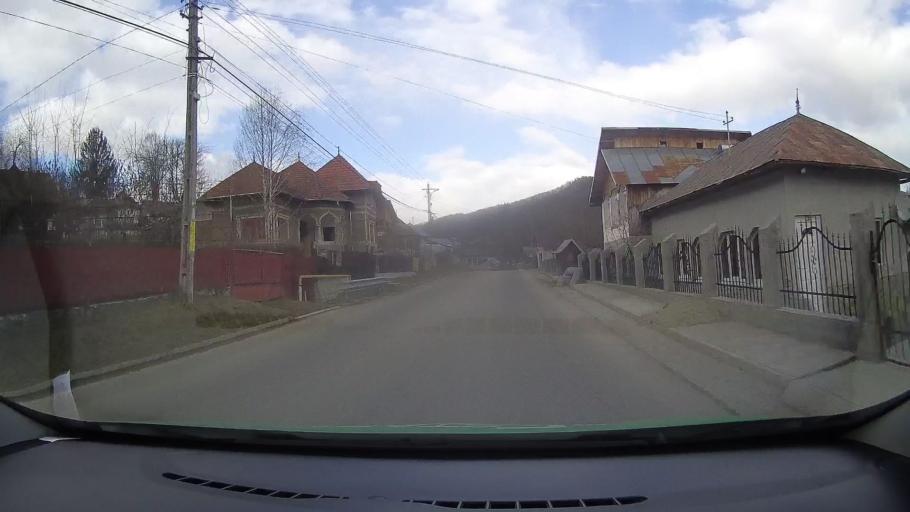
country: RO
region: Dambovita
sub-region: Comuna Visinesti
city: Visinesti
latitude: 45.0733
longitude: 25.5440
